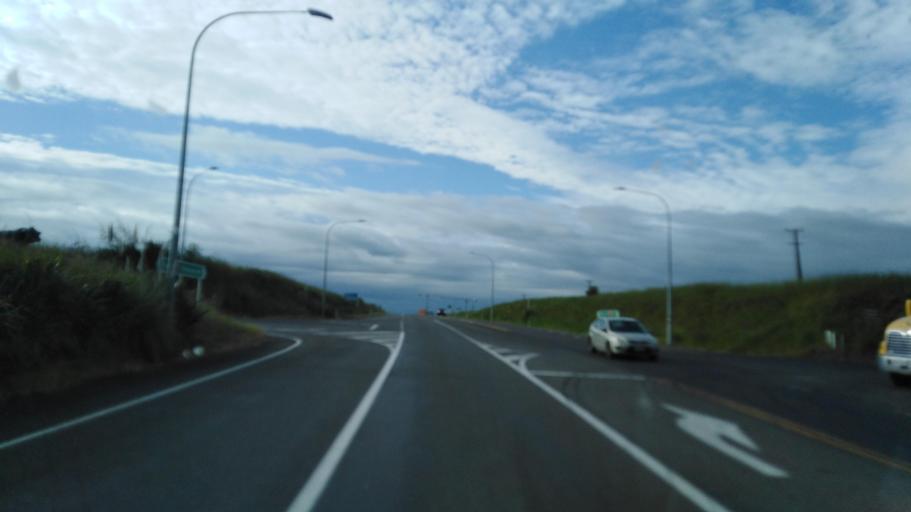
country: NZ
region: Manawatu-Wanganui
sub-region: Rangitikei District
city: Bulls
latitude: -40.1913
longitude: 175.3888
